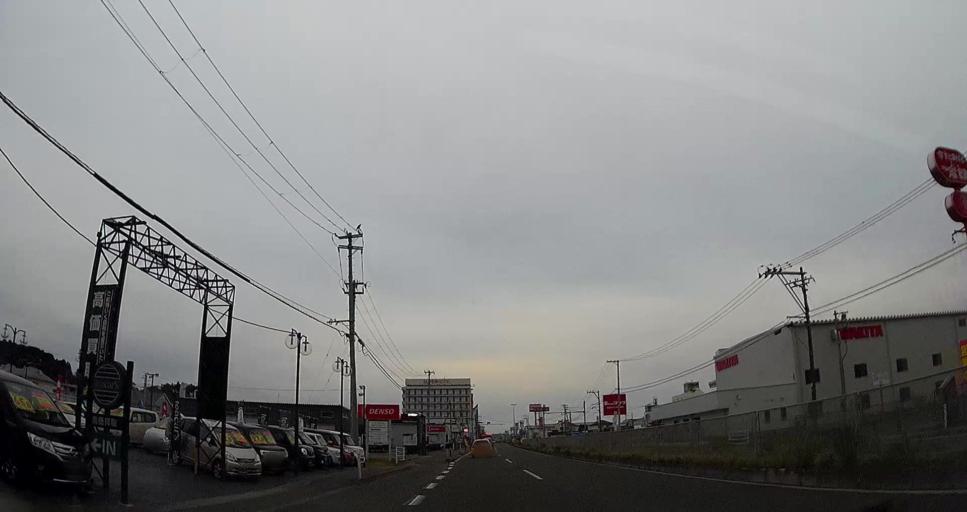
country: JP
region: Miyagi
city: Iwanuma
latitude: 38.1458
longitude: 140.8823
